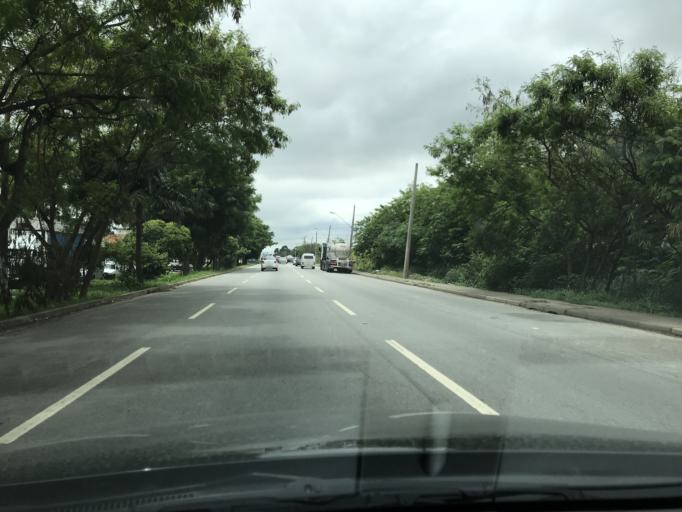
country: BR
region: Sao Paulo
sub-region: Itaquaquecetuba
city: Itaquaquecetuba
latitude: -23.4694
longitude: -46.3327
